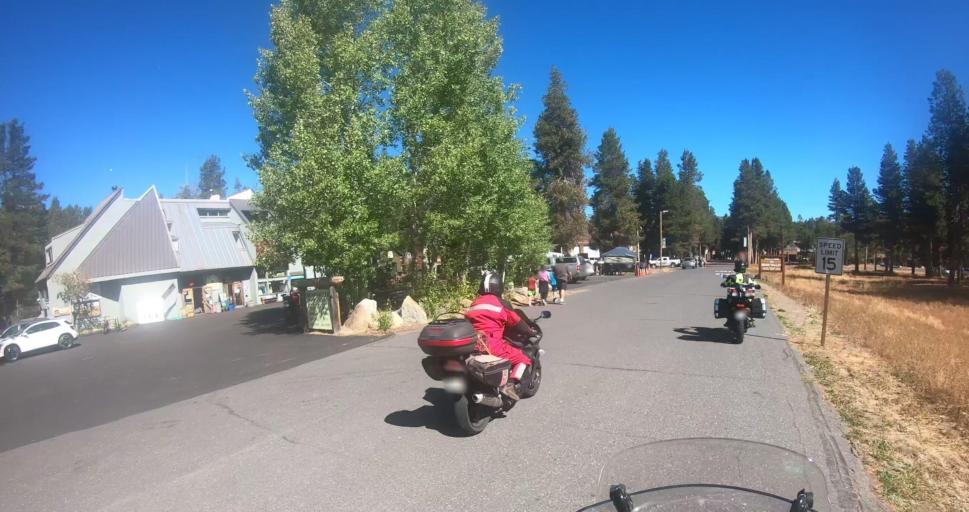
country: US
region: California
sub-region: Calaveras County
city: Arnold
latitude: 38.4618
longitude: -120.0420
